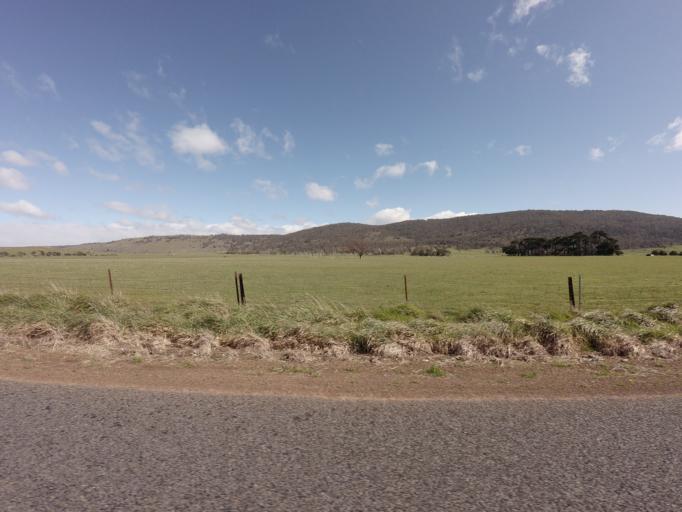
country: AU
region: Tasmania
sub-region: Northern Midlands
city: Evandale
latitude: -41.9849
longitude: 147.4504
